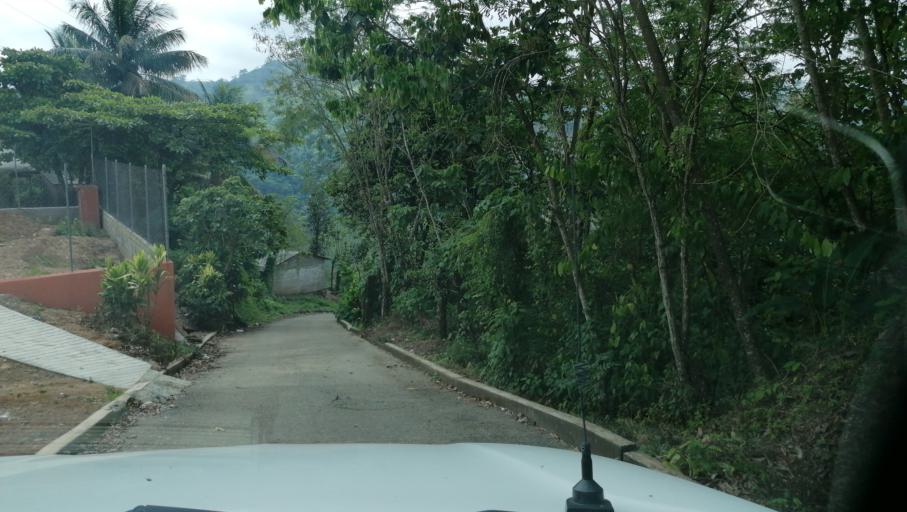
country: MX
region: Chiapas
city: Ixtacomitan
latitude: 17.3576
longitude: -93.1288
